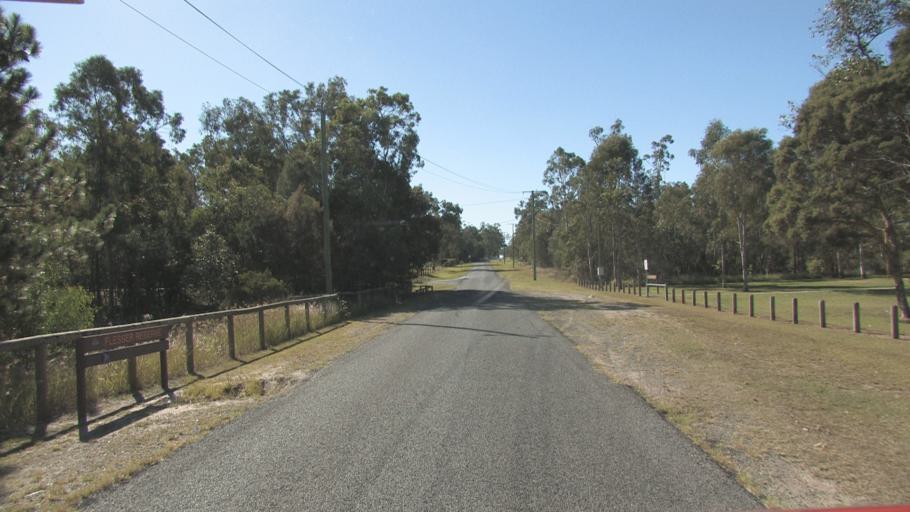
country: AU
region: Queensland
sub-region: Logan
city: Chambers Flat
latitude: -27.7357
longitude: 153.0712
